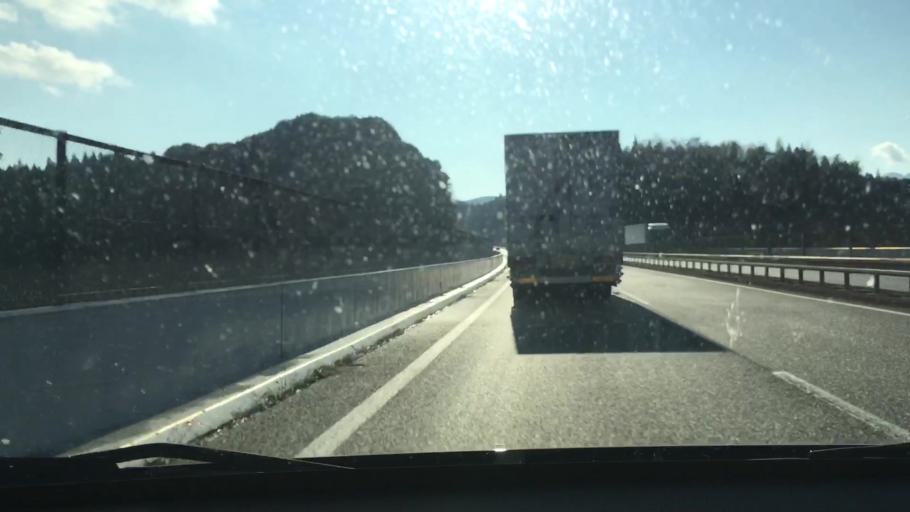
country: JP
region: Kagoshima
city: Okuchi-shinohara
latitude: 31.9400
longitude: 130.7121
